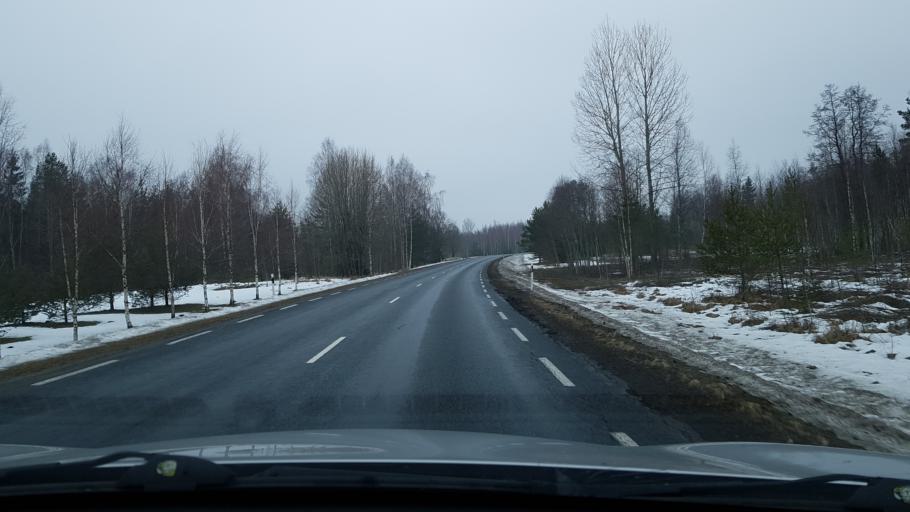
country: EE
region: Valgamaa
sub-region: Torva linn
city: Torva
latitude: 58.1196
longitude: 25.9939
